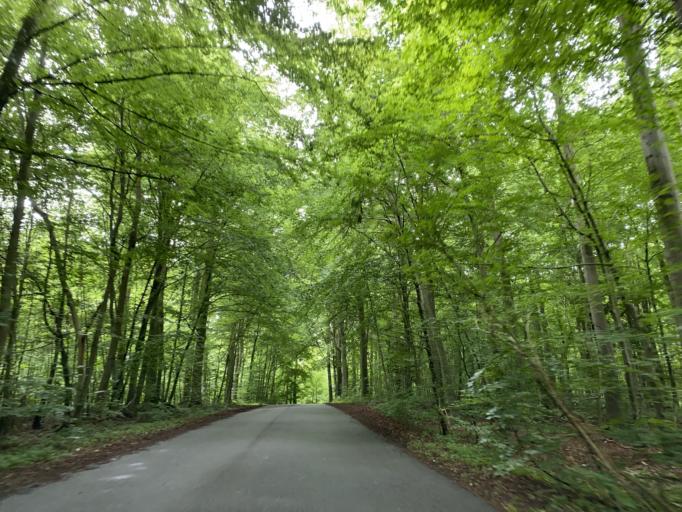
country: DK
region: South Denmark
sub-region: Sonderborg Kommune
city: Sonderborg
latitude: 54.9087
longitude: 9.8323
